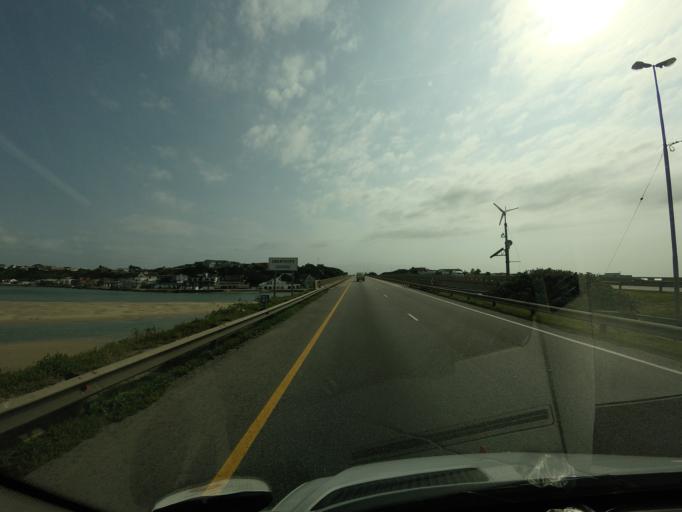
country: ZA
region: Eastern Cape
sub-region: Nelson Mandela Bay Metropolitan Municipality
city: Port Elizabeth
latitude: -33.8650
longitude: 25.6262
